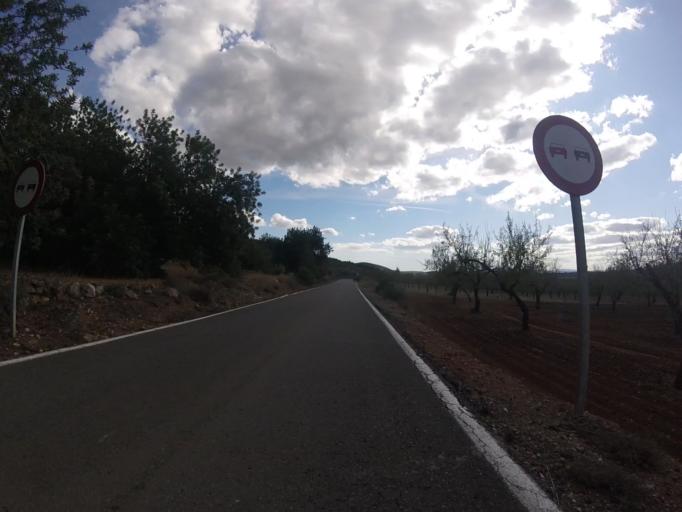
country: ES
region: Valencia
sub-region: Provincia de Castello
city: Cuevas de Vinroma
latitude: 40.3609
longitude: 0.1245
